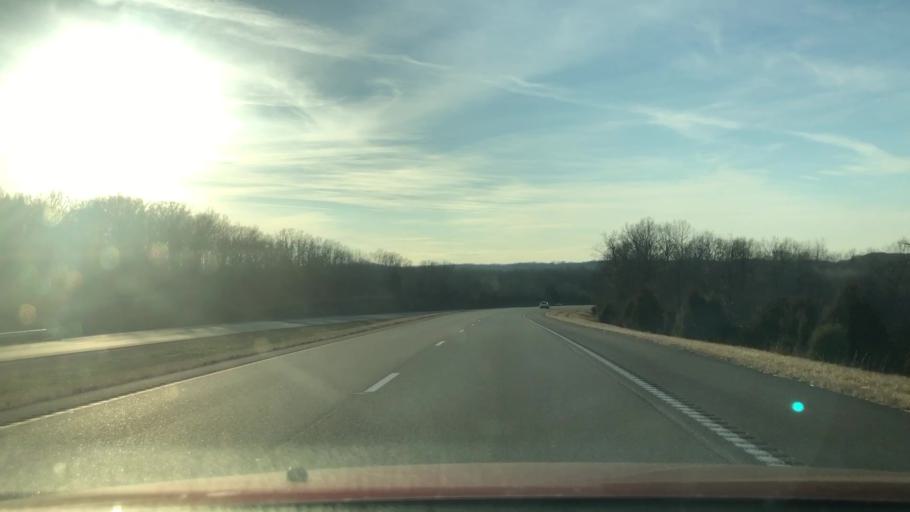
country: US
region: Missouri
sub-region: Wright County
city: Mansfield
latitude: 37.1110
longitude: -92.6403
